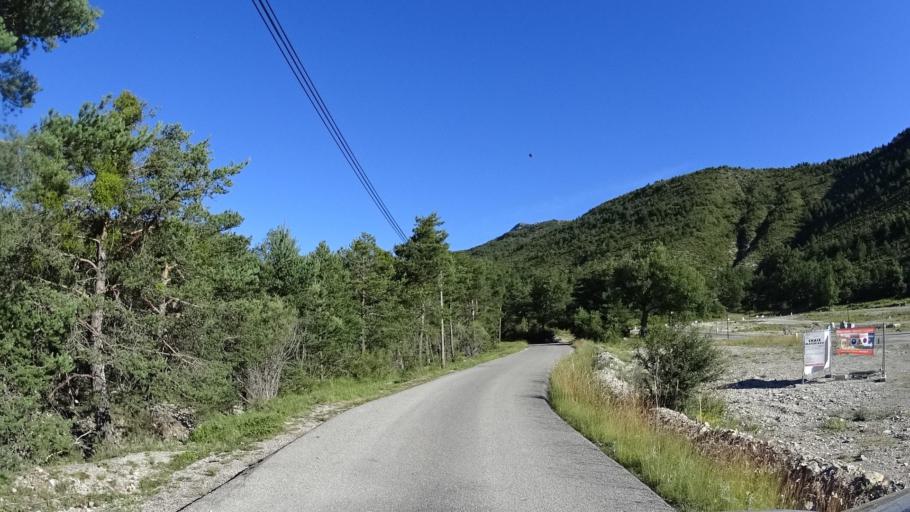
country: FR
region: Provence-Alpes-Cote d'Azur
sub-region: Departement des Alpes-de-Haute-Provence
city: Castellane
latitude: 43.8783
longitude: 6.5035
